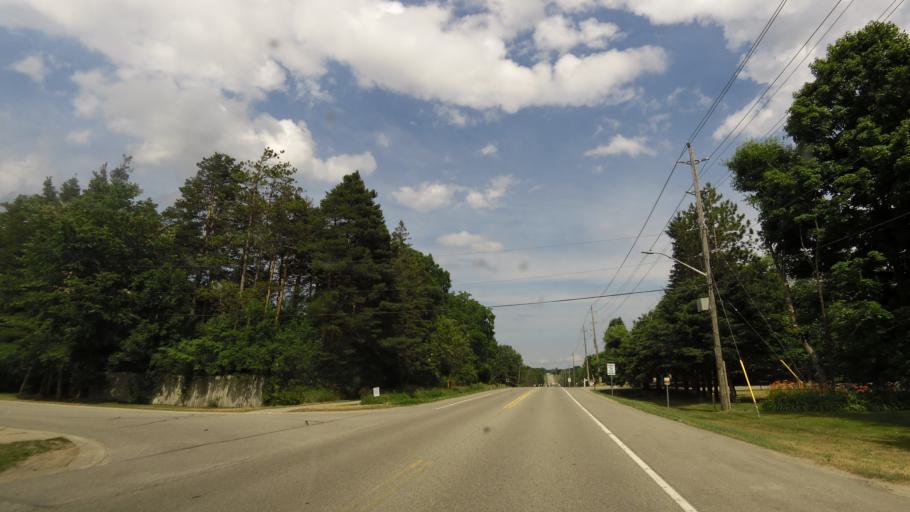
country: CA
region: Ontario
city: Orangeville
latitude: 43.9471
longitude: -80.0996
